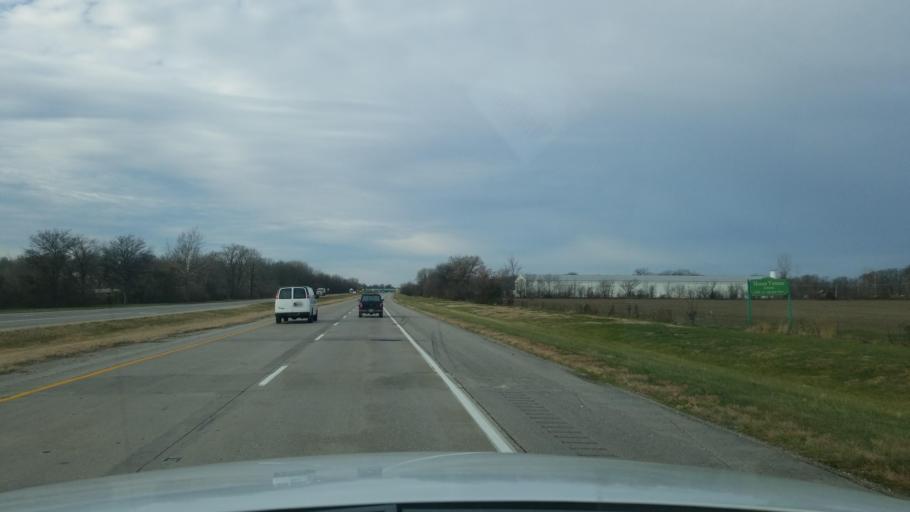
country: US
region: Indiana
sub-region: Posey County
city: Mount Vernon
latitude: 37.9412
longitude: -87.8611
